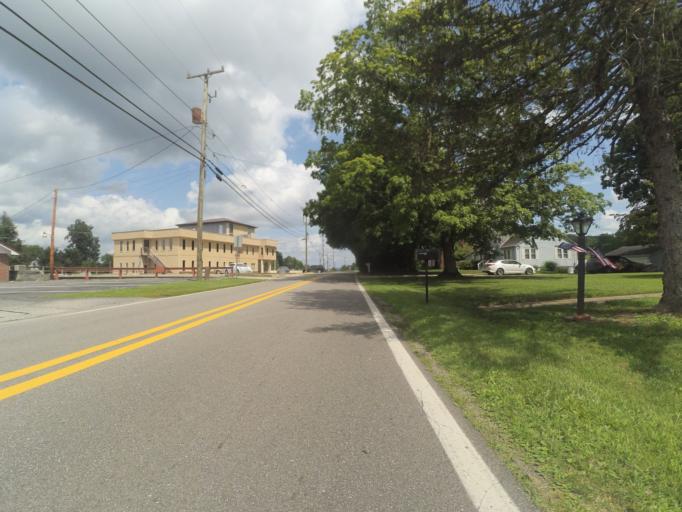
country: US
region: West Virginia
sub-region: Cabell County
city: Pea Ridge
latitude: 38.4096
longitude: -82.3345
